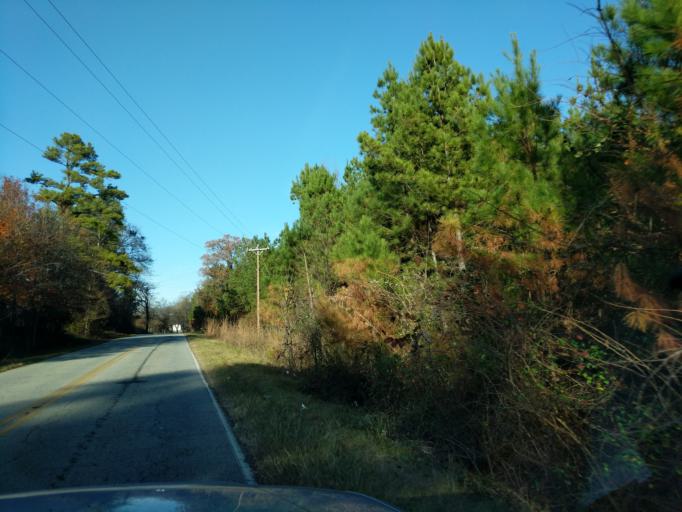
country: US
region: South Carolina
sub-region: Spartanburg County
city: Wellford
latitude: 34.9175
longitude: -82.0823
